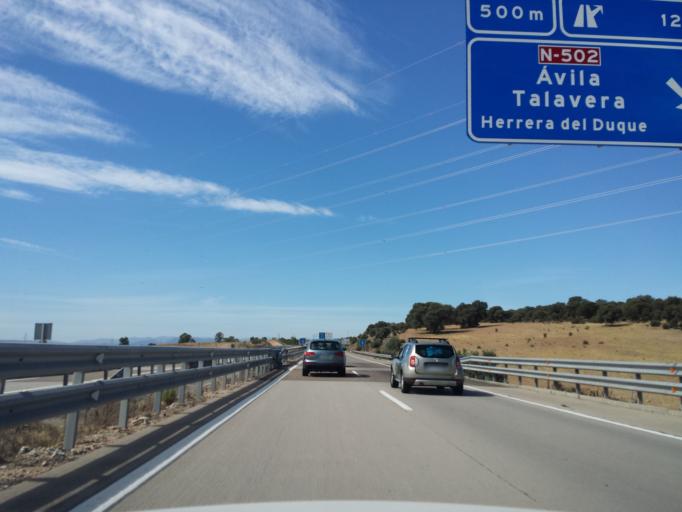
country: ES
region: Castille-La Mancha
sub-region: Province of Toledo
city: Mejorada
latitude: 39.9662
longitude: -4.8975
